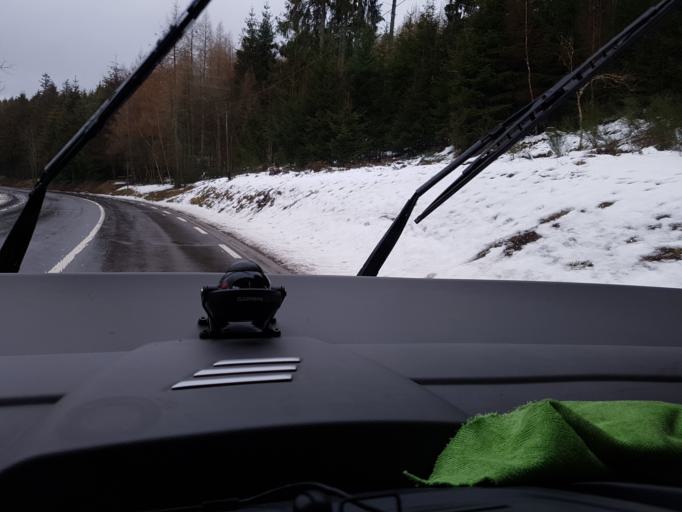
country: FR
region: Lorraine
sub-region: Departement des Vosges
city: Plainfaing
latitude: 48.1762
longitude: 7.0269
